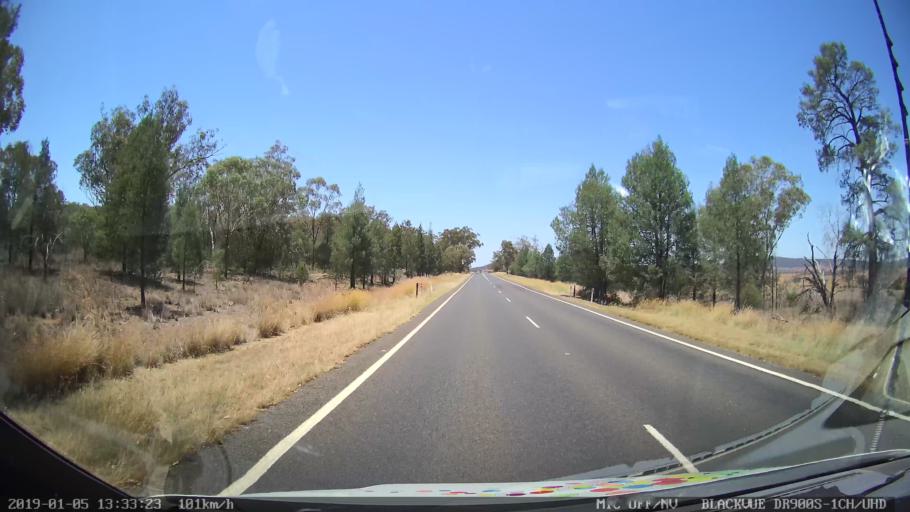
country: AU
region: New South Wales
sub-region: Gunnedah
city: Gunnedah
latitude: -31.0009
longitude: 150.1157
